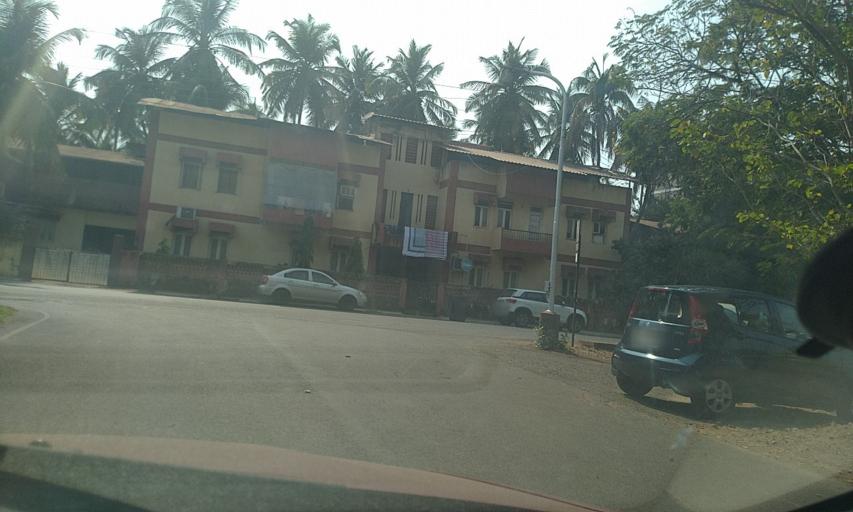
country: IN
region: Goa
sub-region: North Goa
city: Panaji
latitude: 15.4838
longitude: 73.8138
